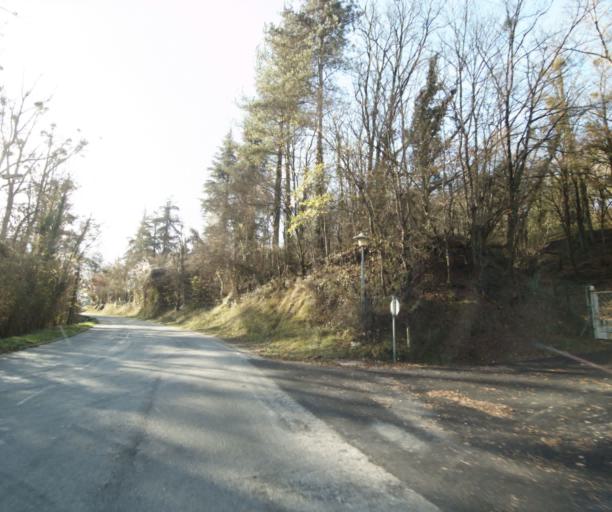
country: FR
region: Poitou-Charentes
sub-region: Departement de la Charente-Maritime
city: Ecoyeux
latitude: 45.7579
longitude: -0.5036
